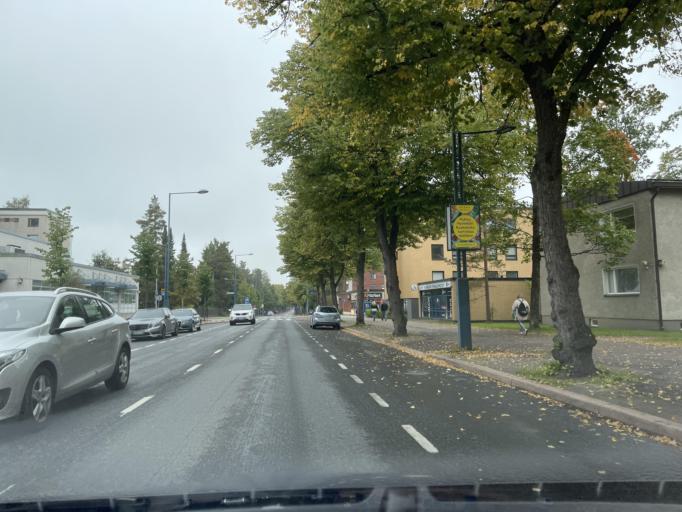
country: FI
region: Uusimaa
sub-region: Helsinki
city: Hyvinge
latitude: 60.6256
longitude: 24.8529
